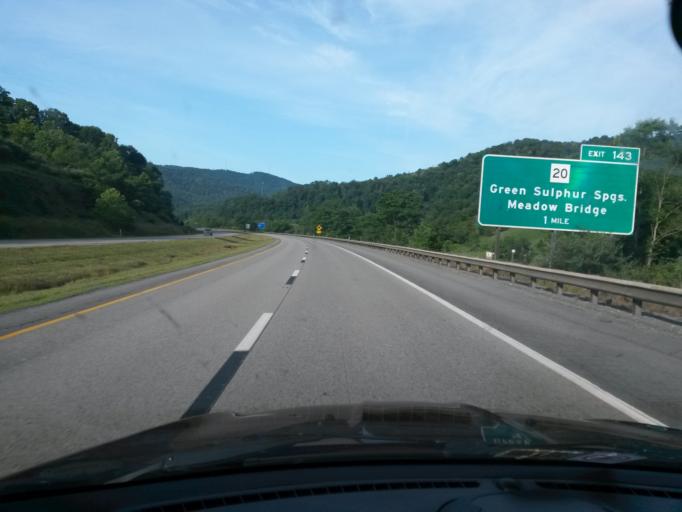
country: US
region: West Virginia
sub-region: Greenbrier County
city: Rainelle
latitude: 37.8225
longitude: -80.8105
